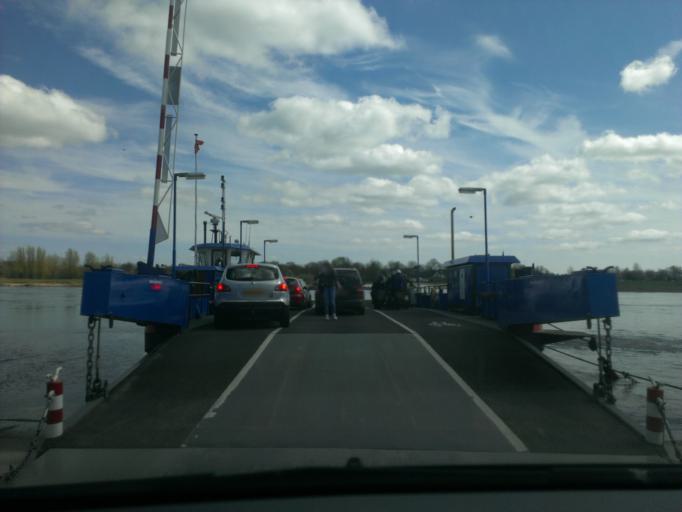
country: NL
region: Overijssel
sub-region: Gemeente Olst-Wijhe
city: Wijhe
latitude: 52.3927
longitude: 6.1241
